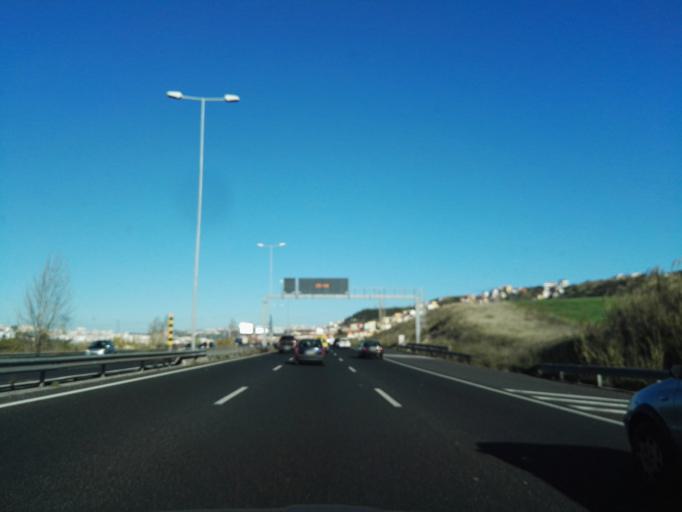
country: PT
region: Lisbon
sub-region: Odivelas
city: Pontinha
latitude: 38.7729
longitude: -9.2004
